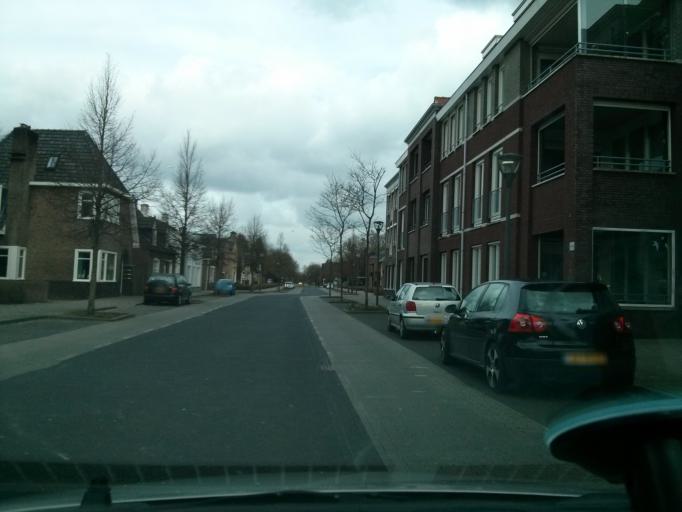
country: NL
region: North Brabant
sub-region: Gemeente Son en Breugel
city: Son
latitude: 51.5129
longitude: 5.4938
